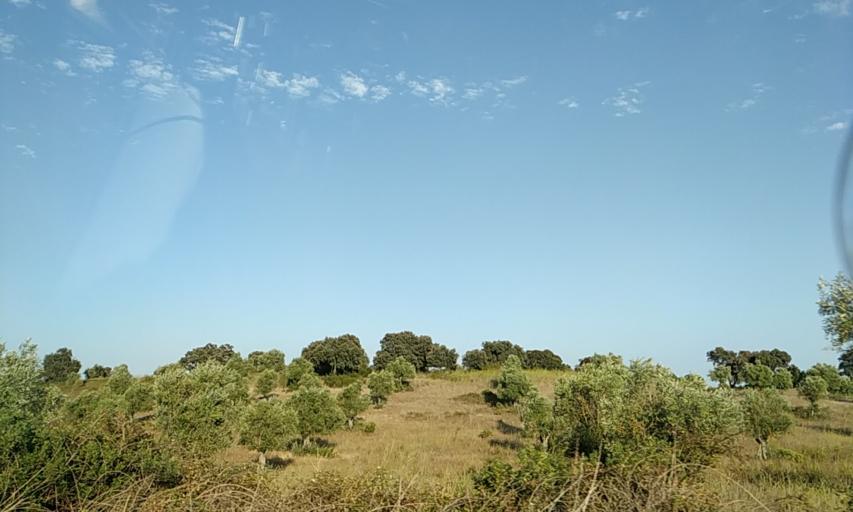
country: PT
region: Santarem
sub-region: Alcanena
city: Alcanena
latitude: 39.3950
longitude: -8.6455
